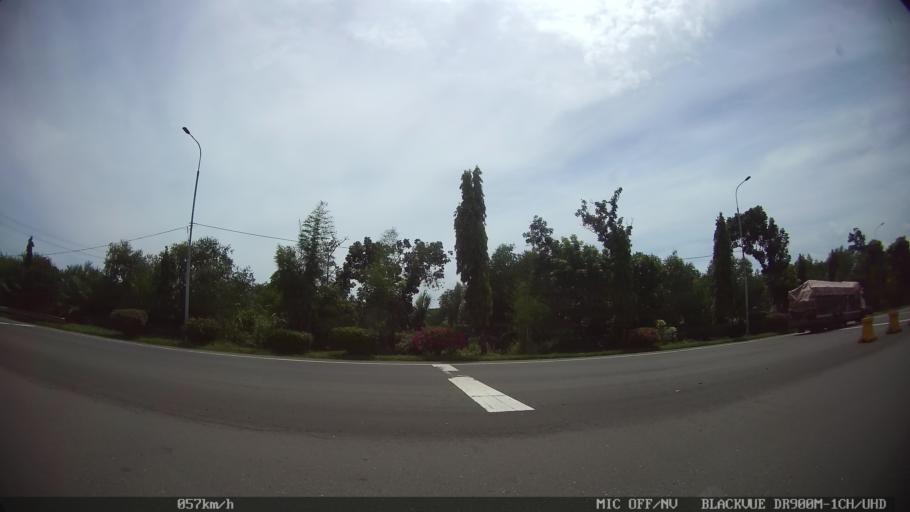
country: ID
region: North Sumatra
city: Labuhan Deli
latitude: 3.7307
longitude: 98.6806
